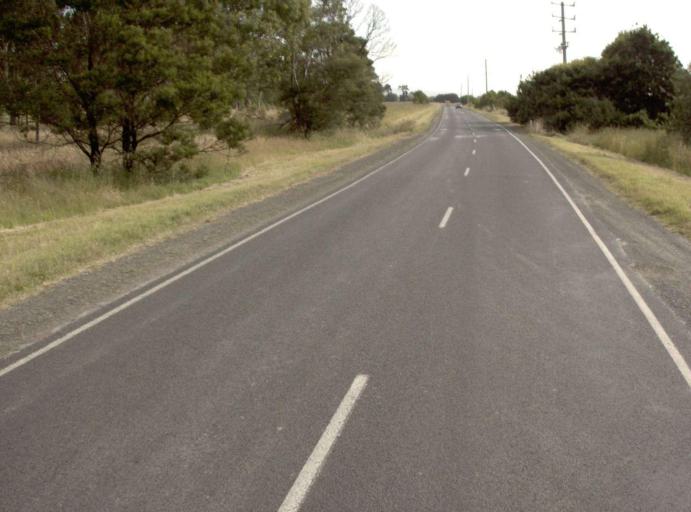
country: AU
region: Victoria
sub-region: Latrobe
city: Traralgon
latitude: -38.0971
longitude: 146.5968
